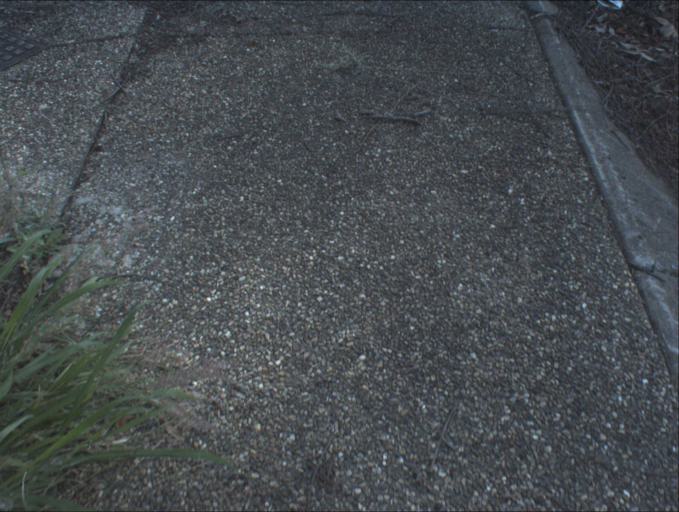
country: AU
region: Queensland
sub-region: Logan
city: Waterford West
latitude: -27.7019
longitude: 153.1640
